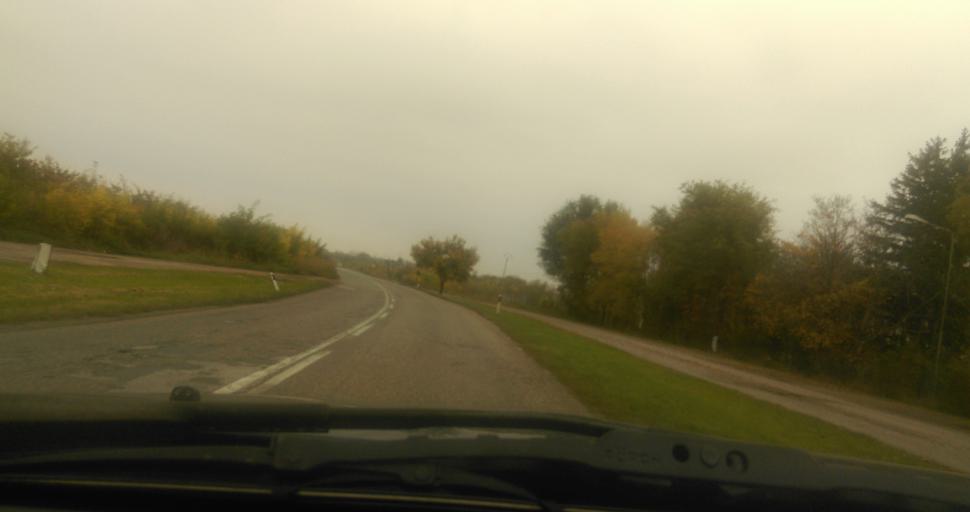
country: RS
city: Backo Gradiste
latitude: 45.5716
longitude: 20.0228
